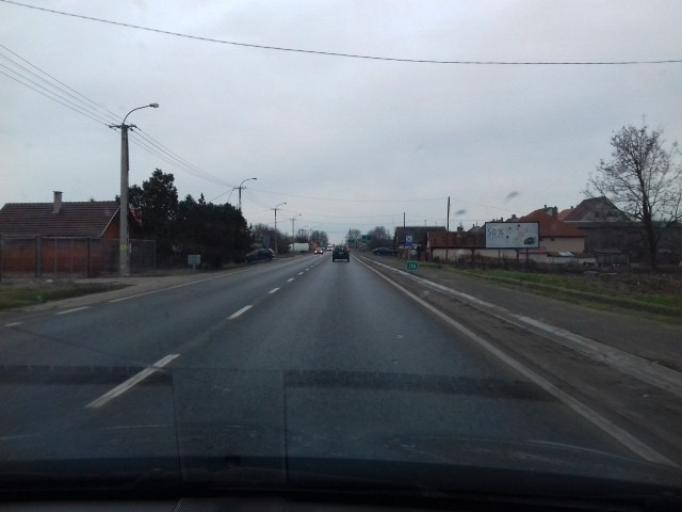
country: HU
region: Szabolcs-Szatmar-Bereg
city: Ujfeherto
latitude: 47.8154
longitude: 21.7010
